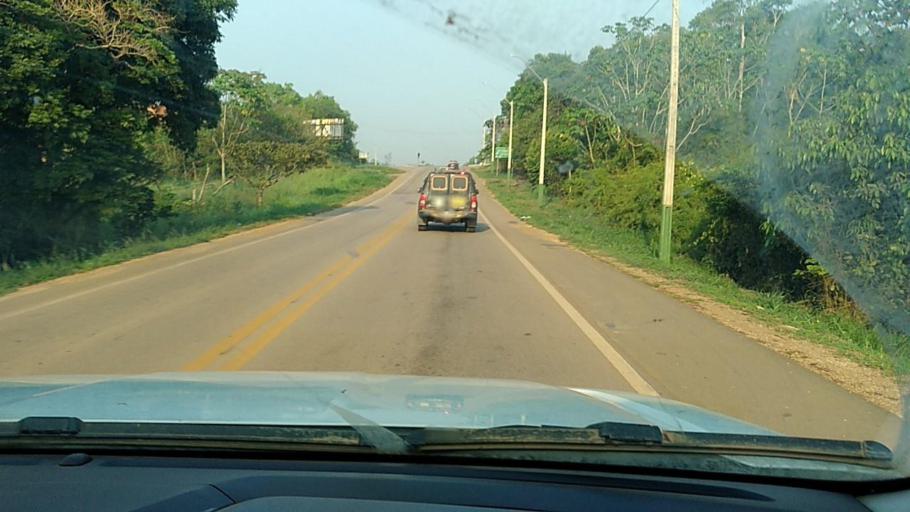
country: BR
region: Rondonia
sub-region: Porto Velho
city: Porto Velho
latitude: -8.7400
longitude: -63.9323
